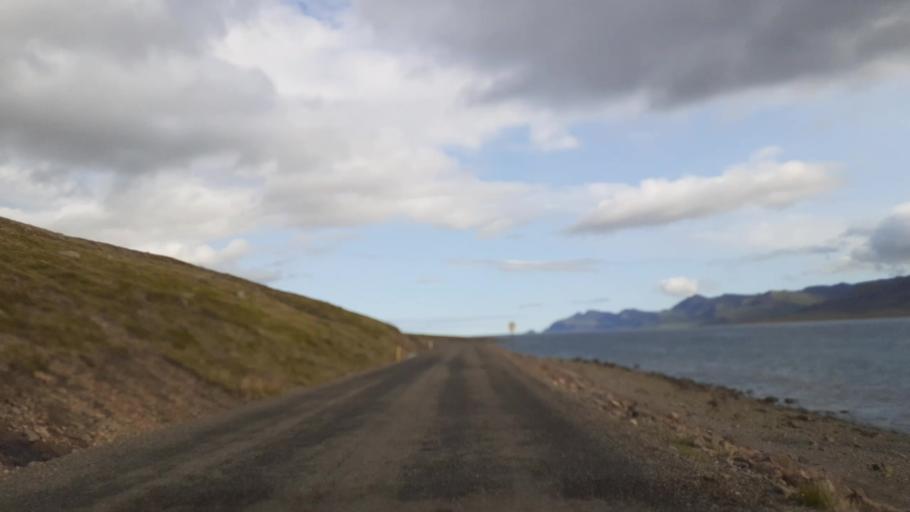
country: IS
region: East
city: Eskifjoerdur
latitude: 65.0593
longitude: -13.9889
